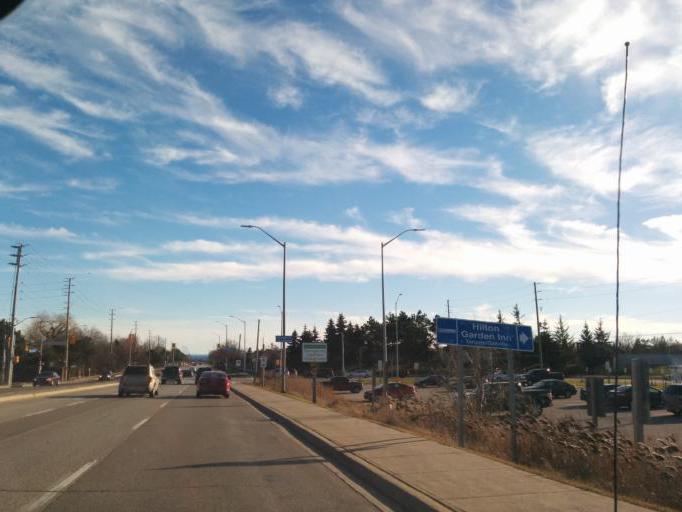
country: CA
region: Ontario
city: Oakville
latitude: 43.5080
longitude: -79.6615
